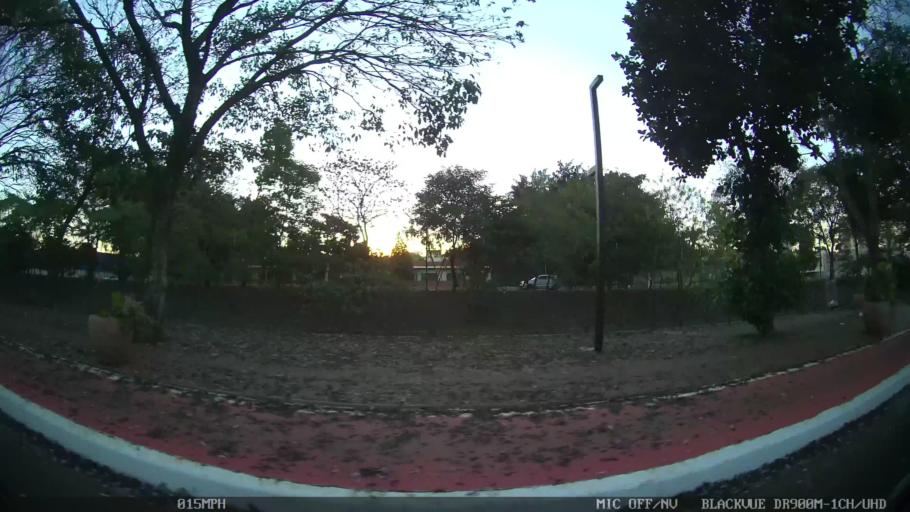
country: BR
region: Sao Paulo
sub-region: Santa Barbara D'Oeste
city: Santa Barbara d'Oeste
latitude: -22.7608
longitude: -47.4111
